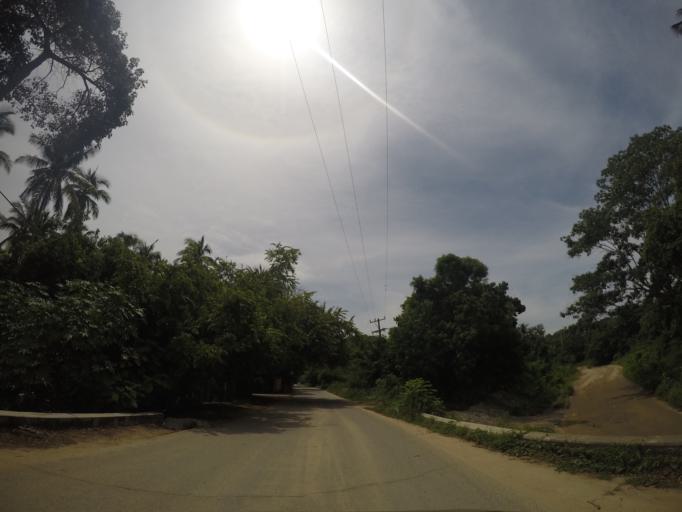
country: MX
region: Oaxaca
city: Santa Maria Tonameca
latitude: 15.6655
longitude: -96.5160
